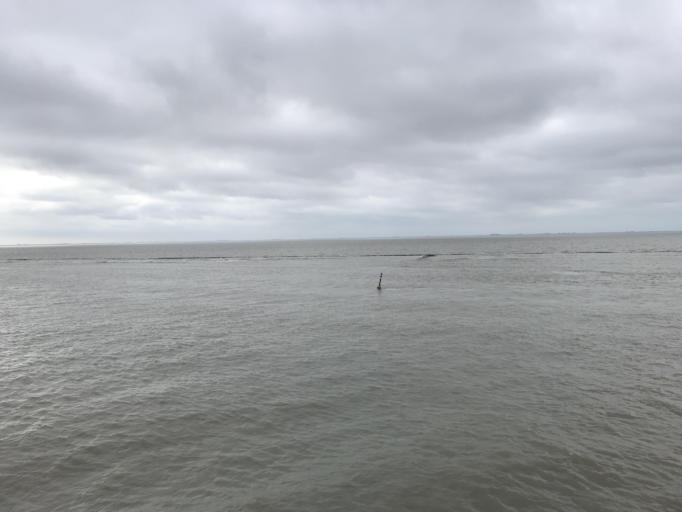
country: DE
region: Lower Saxony
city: Emden
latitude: 53.3302
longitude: 7.1135
